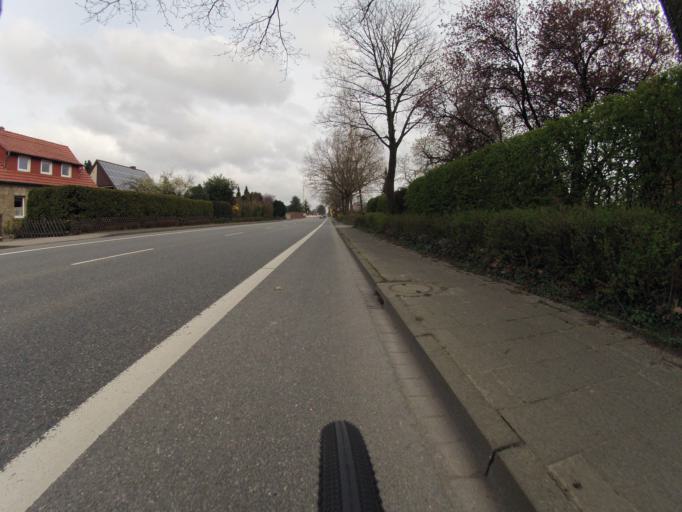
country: DE
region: North Rhine-Westphalia
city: Ibbenburen
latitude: 52.2927
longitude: 7.7093
